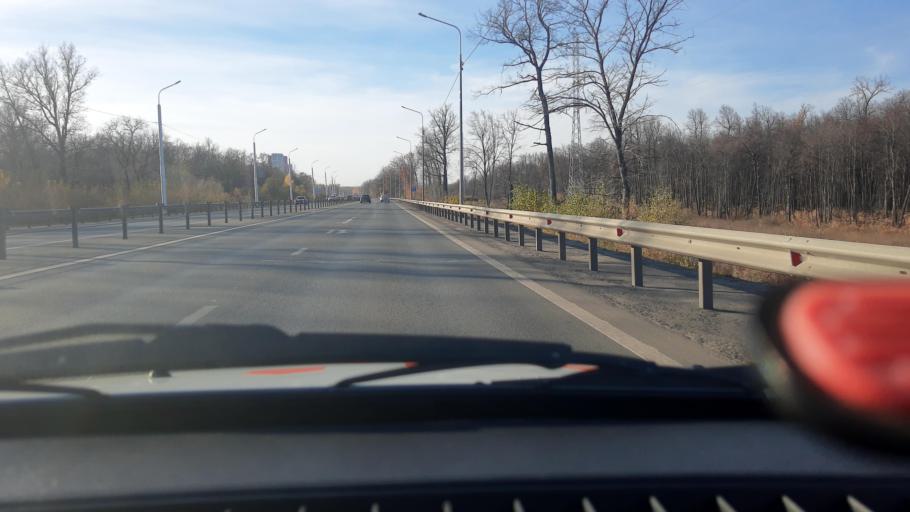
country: RU
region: Bashkortostan
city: Ufa
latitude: 54.6988
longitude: 55.8854
